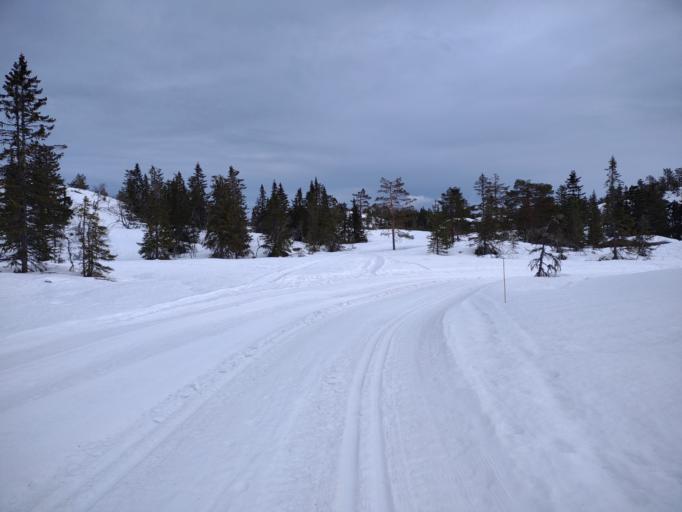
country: NO
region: Buskerud
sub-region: Flesberg
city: Lampeland
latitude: 59.7606
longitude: 9.4504
